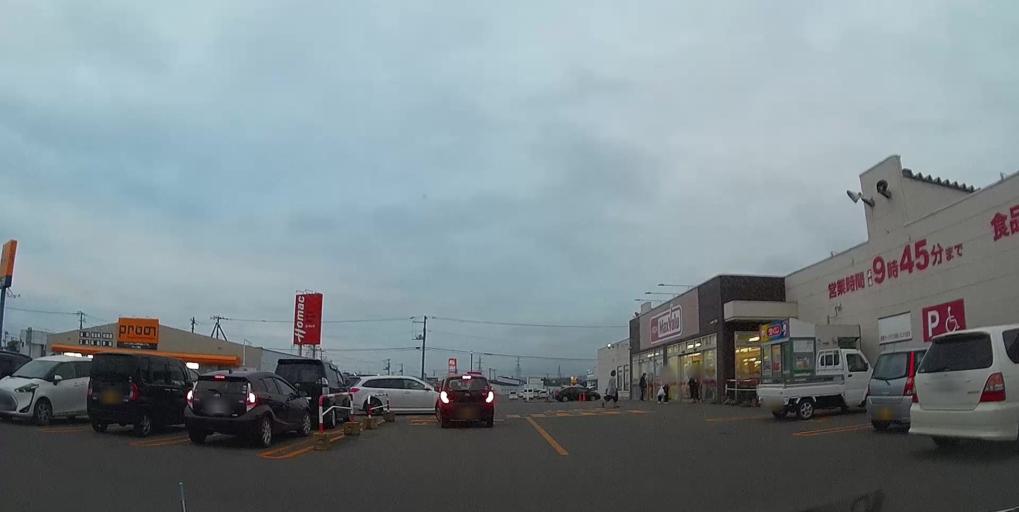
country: JP
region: Hokkaido
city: Nanae
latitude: 42.2504
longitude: 140.2839
